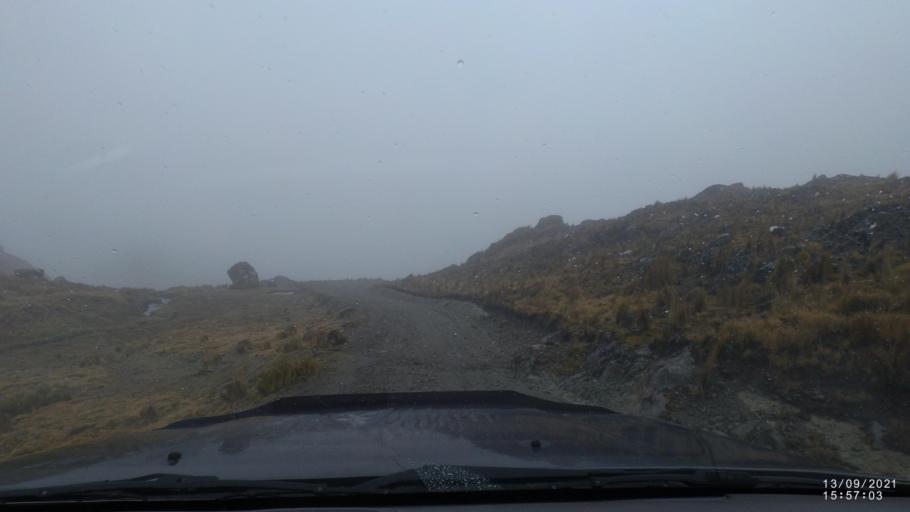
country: BO
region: Cochabamba
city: Colomi
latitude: -17.3025
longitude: -65.7064
